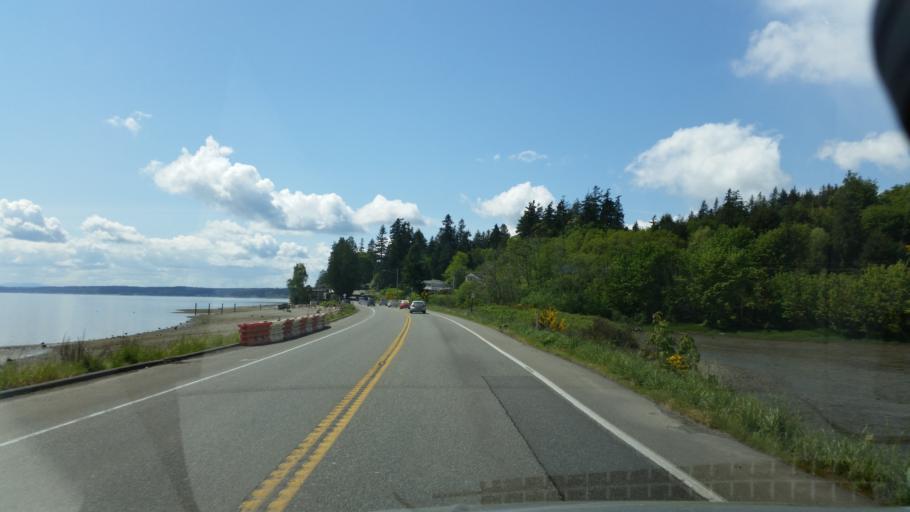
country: US
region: Washington
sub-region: Pierce County
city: Wauna
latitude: 47.3806
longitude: -122.6386
